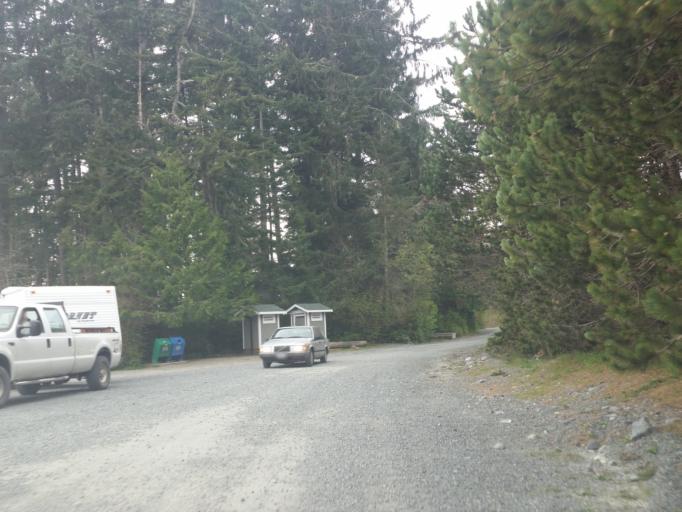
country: CA
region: British Columbia
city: Sooke
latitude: 48.4212
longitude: -124.0526
